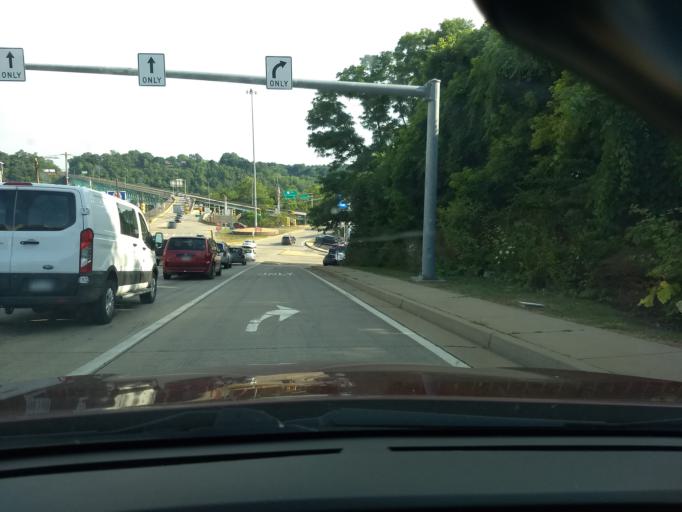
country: US
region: Pennsylvania
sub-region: Allegheny County
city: Tarentum
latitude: 40.6026
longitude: -79.7574
